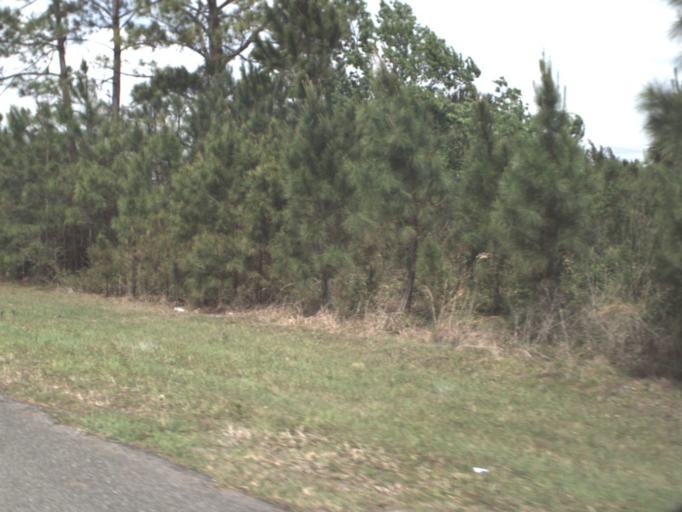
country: US
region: Florida
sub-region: Flagler County
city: Bunnell
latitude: 29.3487
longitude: -81.3111
